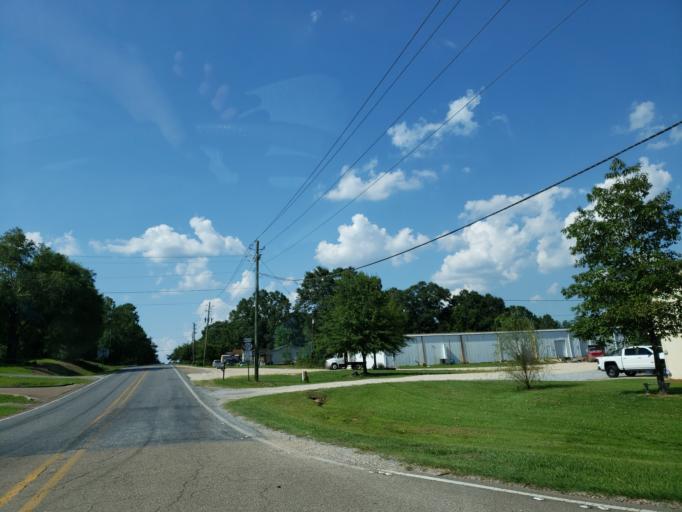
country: US
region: Mississippi
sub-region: Covington County
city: Collins
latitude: 31.5619
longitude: -89.4925
